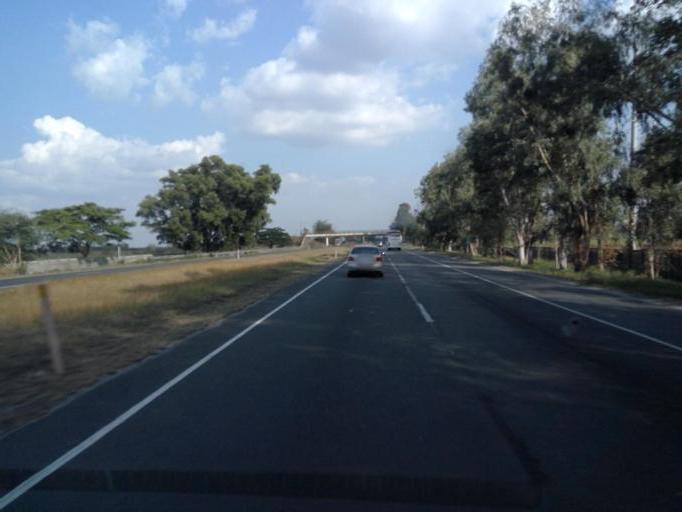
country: PH
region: Central Luzon
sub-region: Province of Pampanga
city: Acli
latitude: 15.1343
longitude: 120.6393
